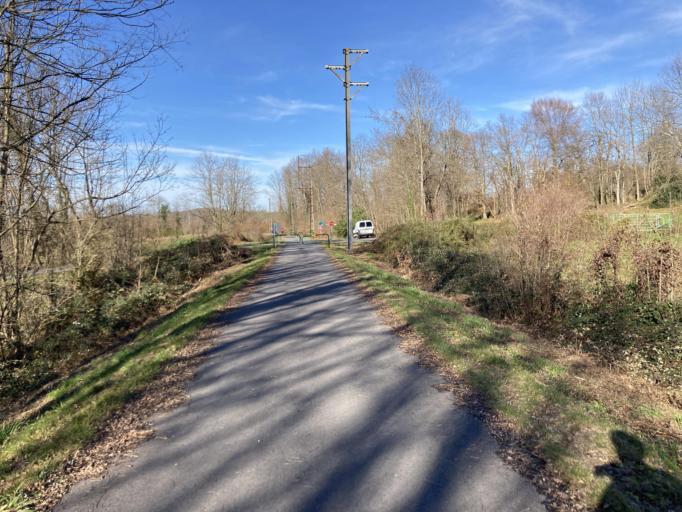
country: FR
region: Aquitaine
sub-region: Departement des Pyrenees-Atlantiques
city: Arudy
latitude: 43.1377
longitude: -0.4475
